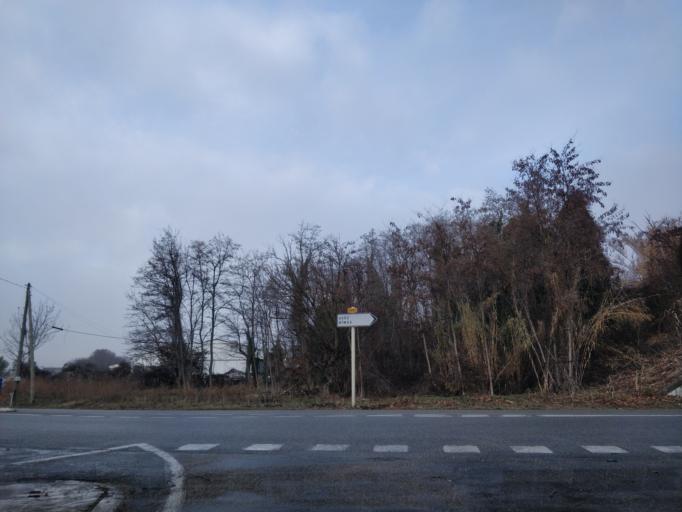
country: FR
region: Languedoc-Roussillon
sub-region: Departement du Gard
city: Saint-Mamert-du-Gard
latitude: 43.9023
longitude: 4.2099
